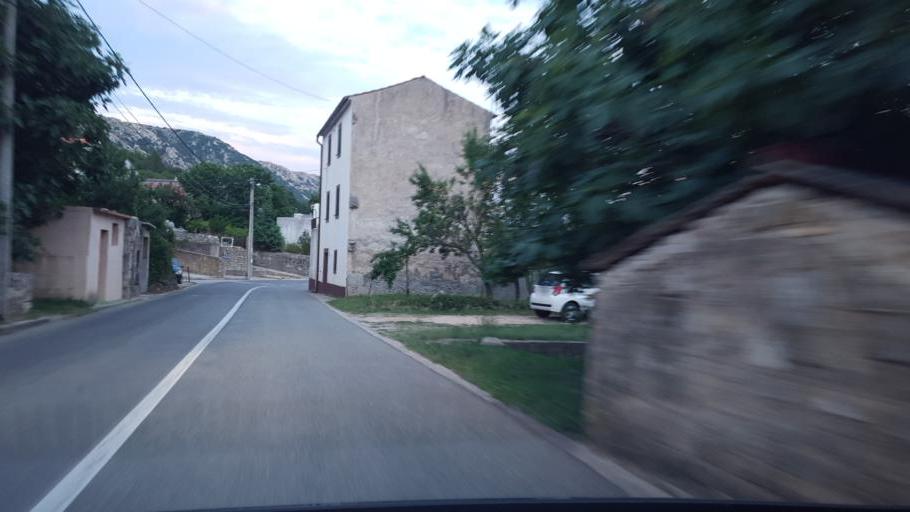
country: HR
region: Primorsko-Goranska
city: Punat
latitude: 44.9990
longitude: 14.7107
